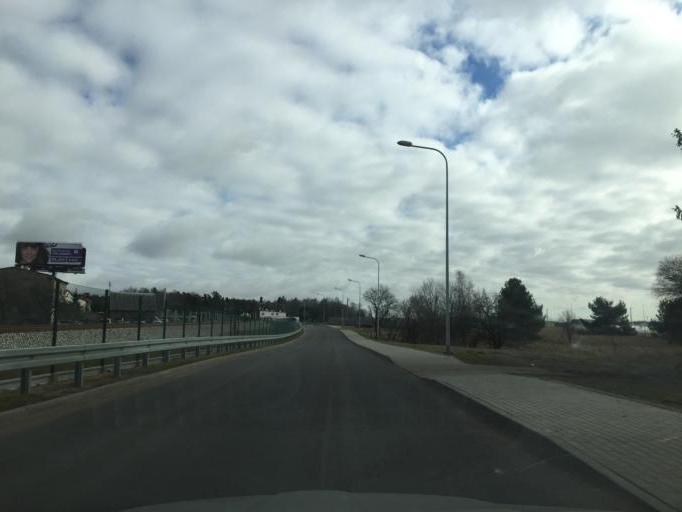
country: PL
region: Pomeranian Voivodeship
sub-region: Powiat kartuski
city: Banino
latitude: 54.3802
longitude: 18.4805
